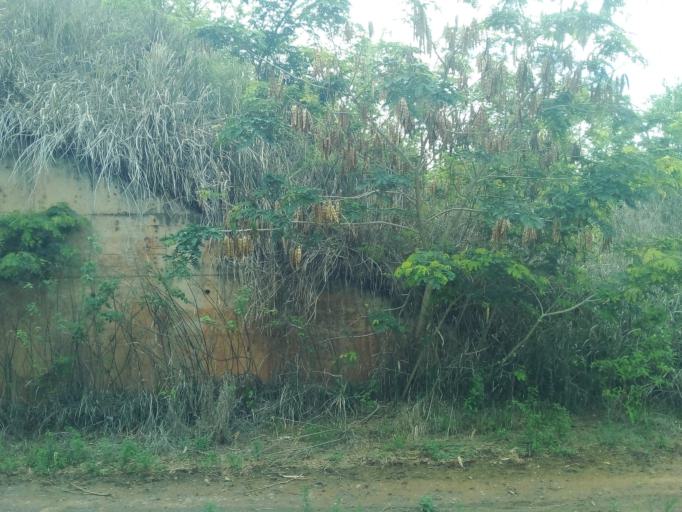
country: BR
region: Minas Gerais
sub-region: Governador Valadares
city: Governador Valadares
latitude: -19.0817
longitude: -42.1608
